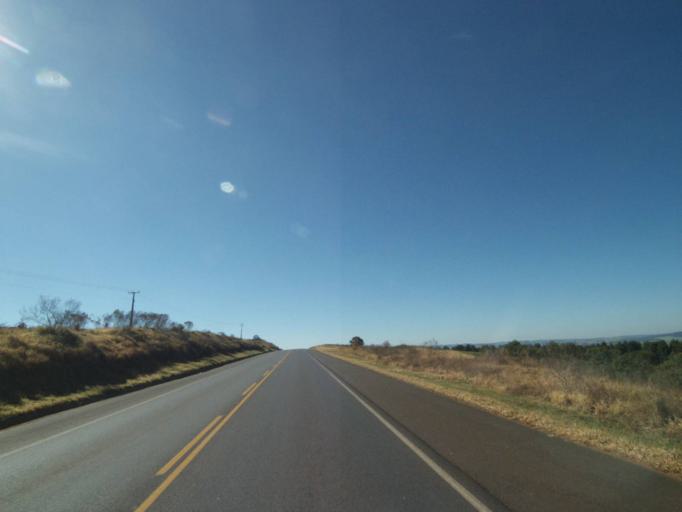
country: BR
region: Parana
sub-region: Tibagi
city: Tibagi
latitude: -24.3648
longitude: -50.3231
